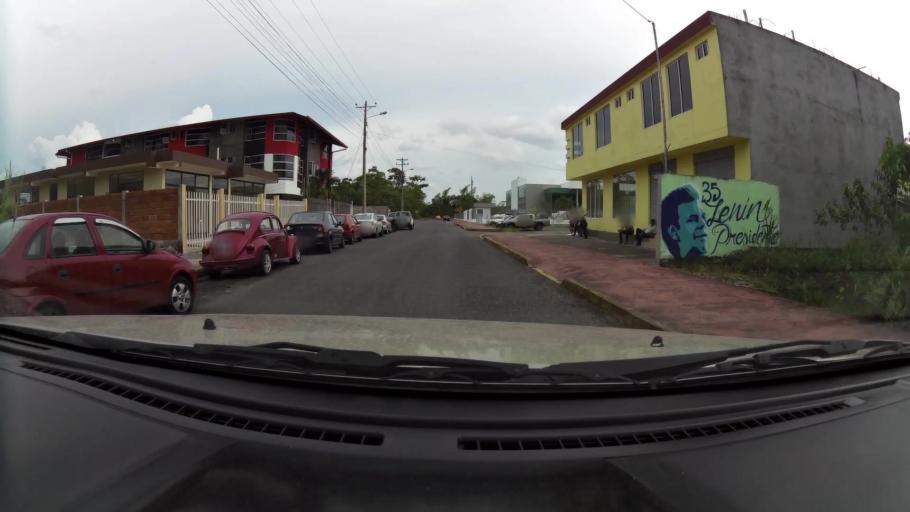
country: EC
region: Pastaza
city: Puyo
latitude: -1.5013
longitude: -78.0211
